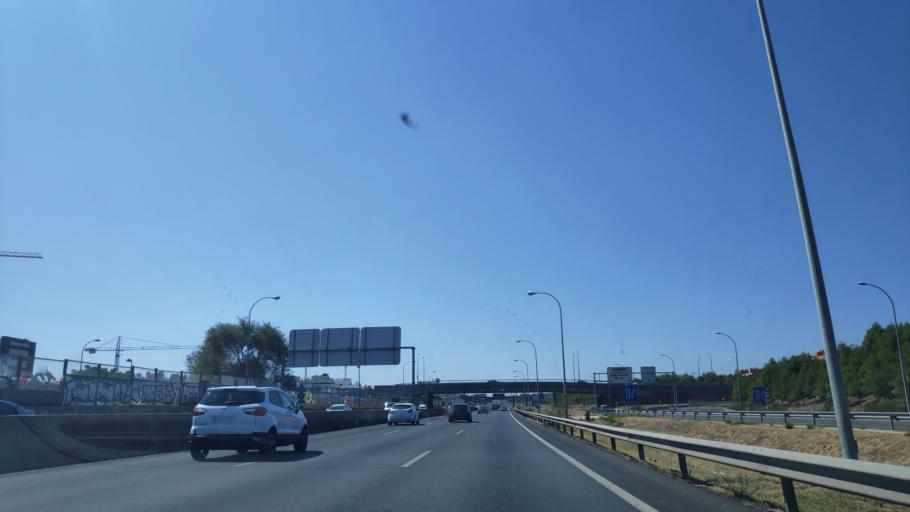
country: ES
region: Madrid
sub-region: Provincia de Madrid
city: Getafe
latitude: 40.3215
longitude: -3.7317
